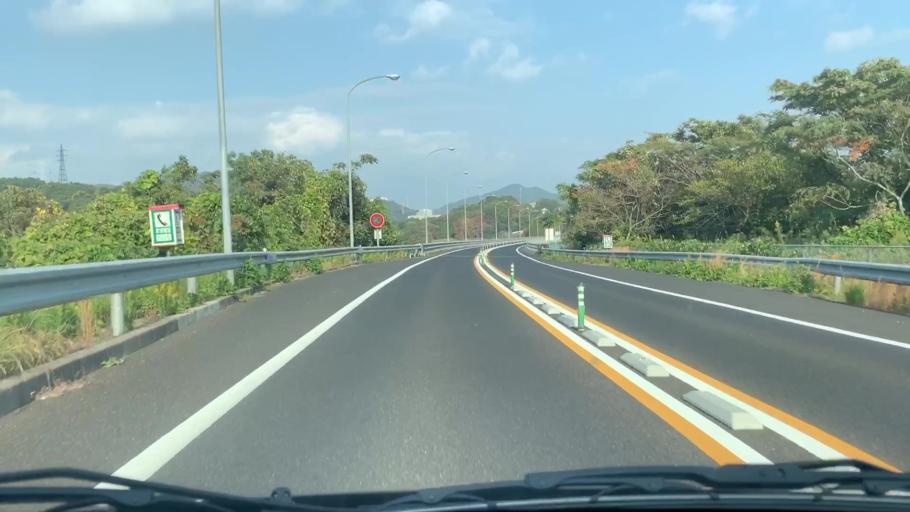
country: JP
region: Nagasaki
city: Sasebo
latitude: 33.0766
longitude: 129.7693
